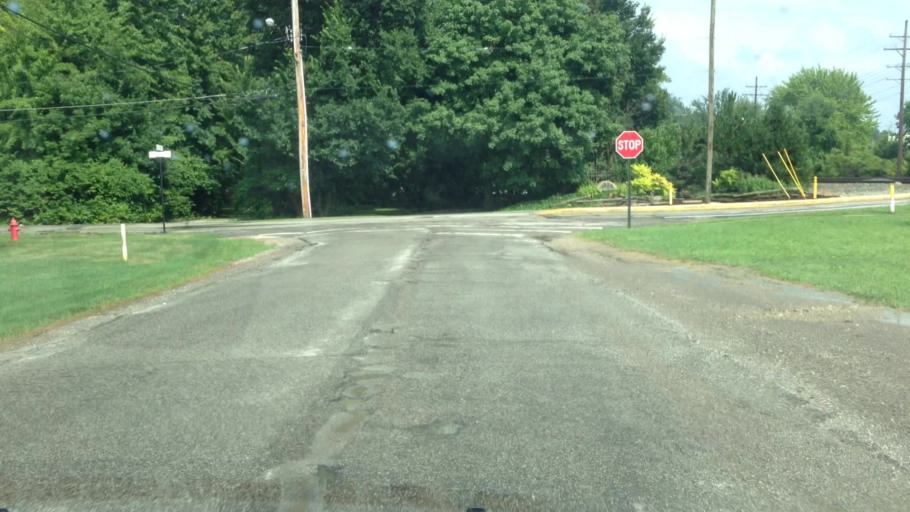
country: US
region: Ohio
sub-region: Cuyahoga County
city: Olmsted Falls
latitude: 41.3755
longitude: -81.9054
